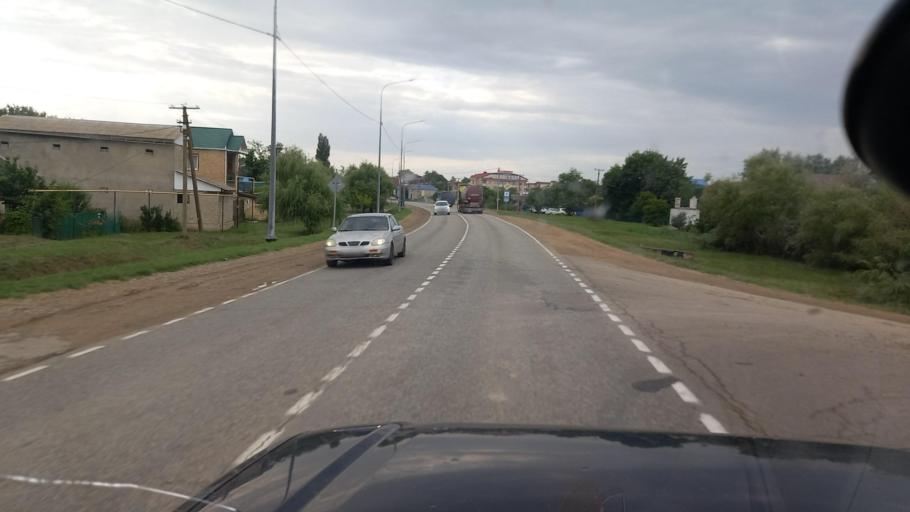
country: RU
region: Krasnodarskiy
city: Akhtanizovskaya
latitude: 45.3469
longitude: 37.1390
